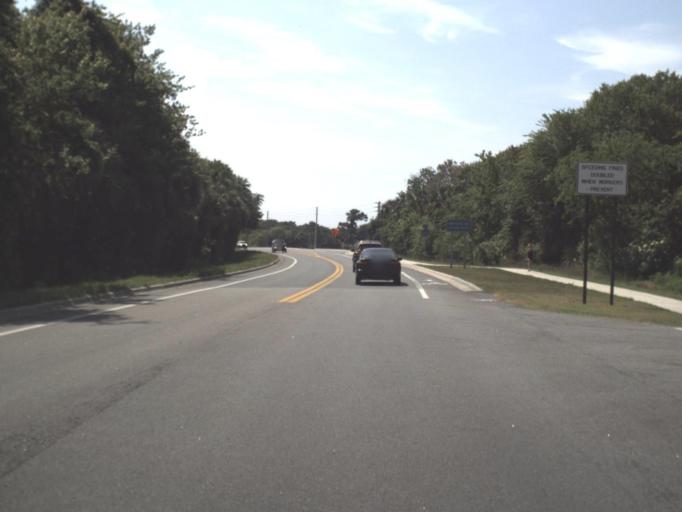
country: US
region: Florida
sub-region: Saint Johns County
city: Palm Valley
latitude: 30.1630
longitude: -81.3632
